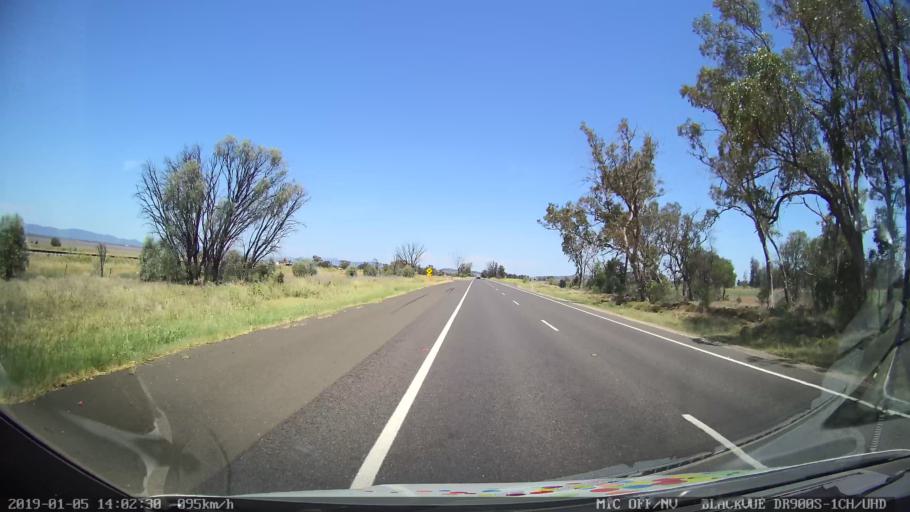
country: AU
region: New South Wales
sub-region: Gunnedah
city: Gunnedah
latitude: -31.1803
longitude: 150.3386
